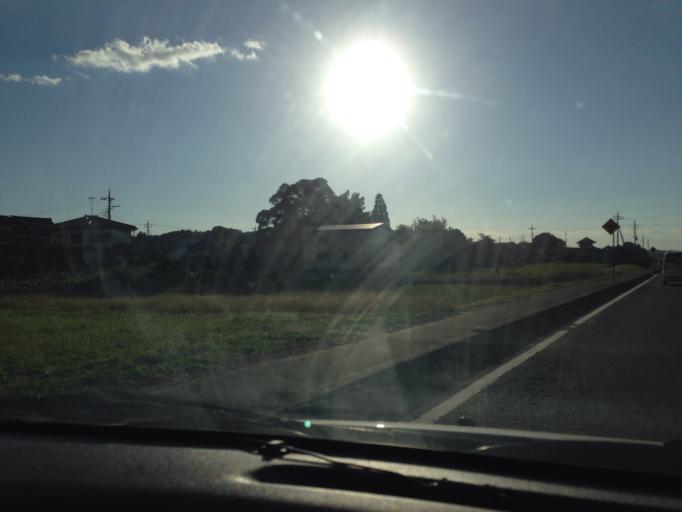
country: JP
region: Ibaraki
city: Inashiki
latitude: 36.0238
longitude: 140.3162
